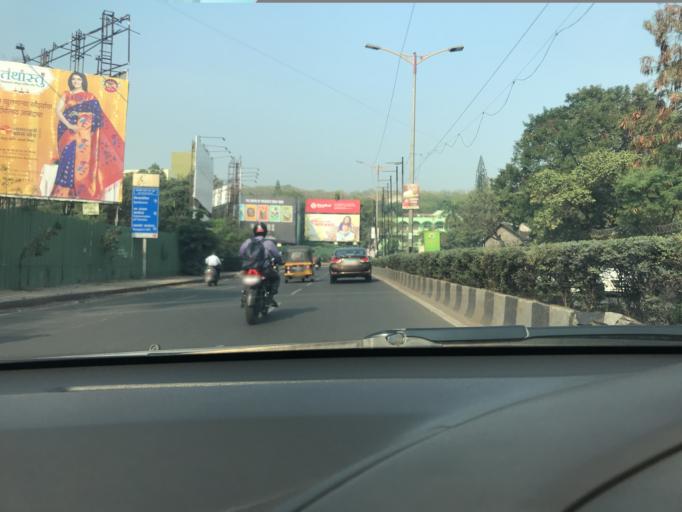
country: IN
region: Maharashtra
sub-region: Pune Division
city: Shivaji Nagar
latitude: 18.5202
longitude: 73.8301
